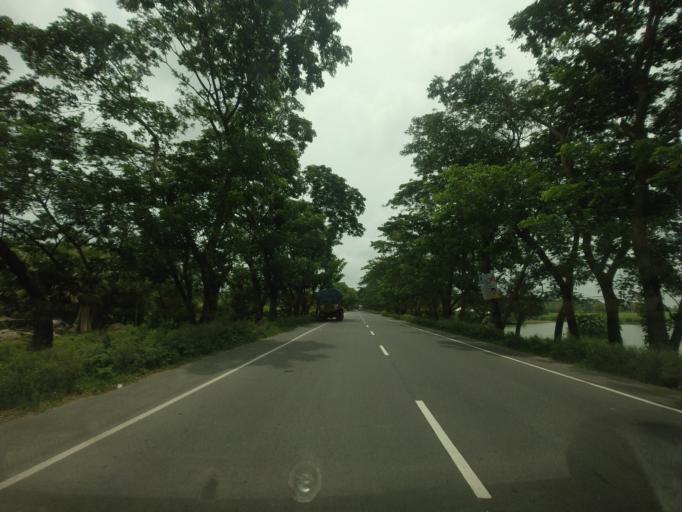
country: BD
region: Khulna
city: Kalia
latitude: 23.2200
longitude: 89.7247
